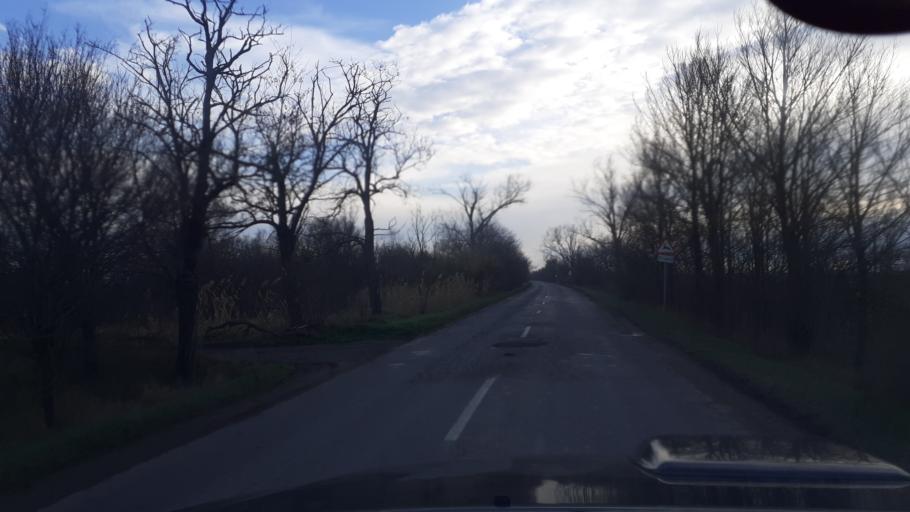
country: HU
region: Bacs-Kiskun
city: Kunszentmiklos
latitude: 46.9568
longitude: 19.1638
